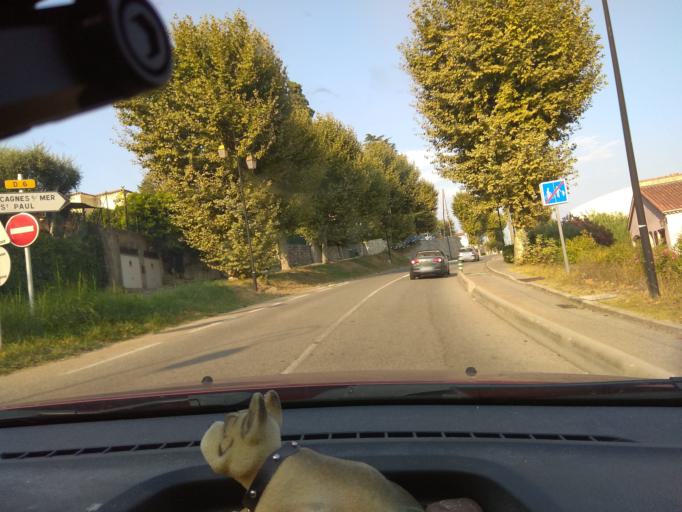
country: FR
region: Provence-Alpes-Cote d'Azur
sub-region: Departement des Alpes-Maritimes
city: La Colle-sur-Loup
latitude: 43.6852
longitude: 7.0965
